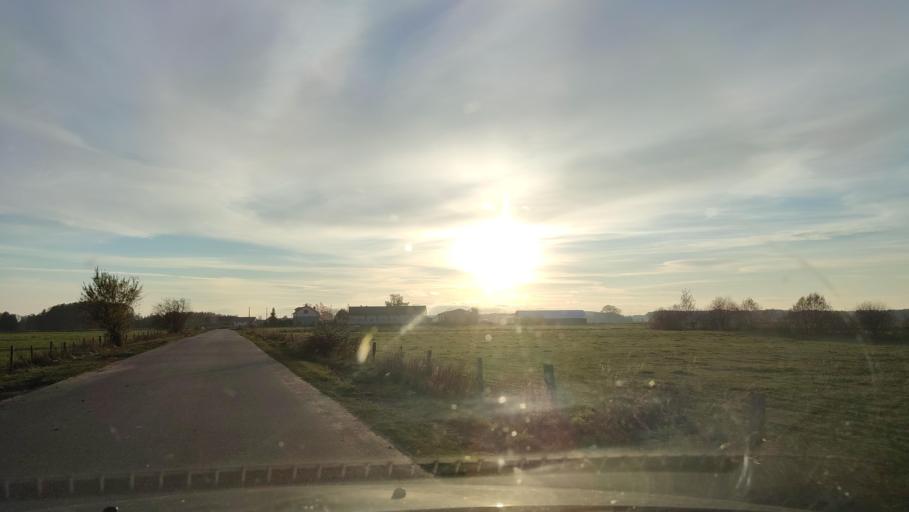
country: PL
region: Masovian Voivodeship
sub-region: Powiat mlawski
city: Dzierzgowo
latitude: 53.2844
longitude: 20.6550
